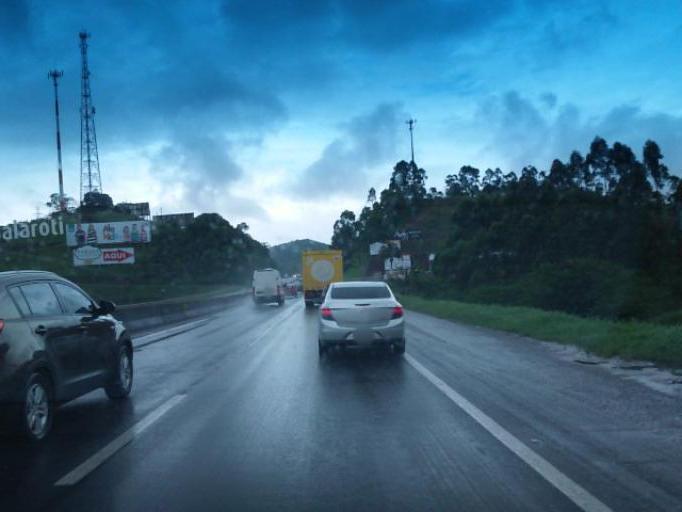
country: BR
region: Santa Catarina
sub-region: Balneario Camboriu
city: Balneario Camboriu
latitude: -26.9754
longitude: -48.6825
